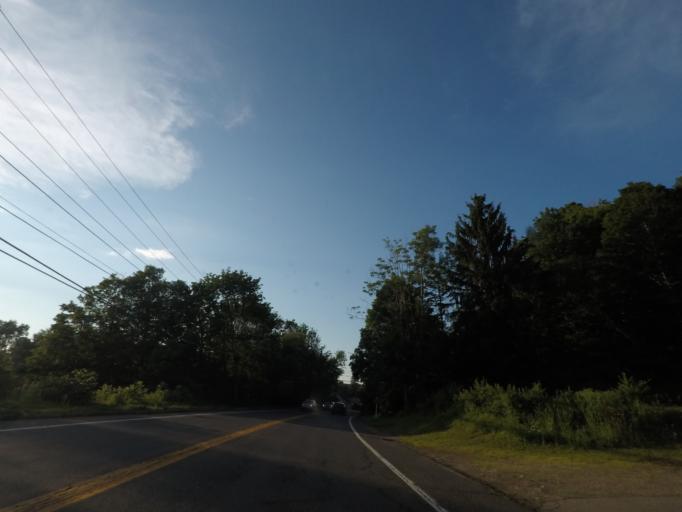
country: US
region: Massachusetts
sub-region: Hampden County
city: Brimfield
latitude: 42.1180
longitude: -72.1984
